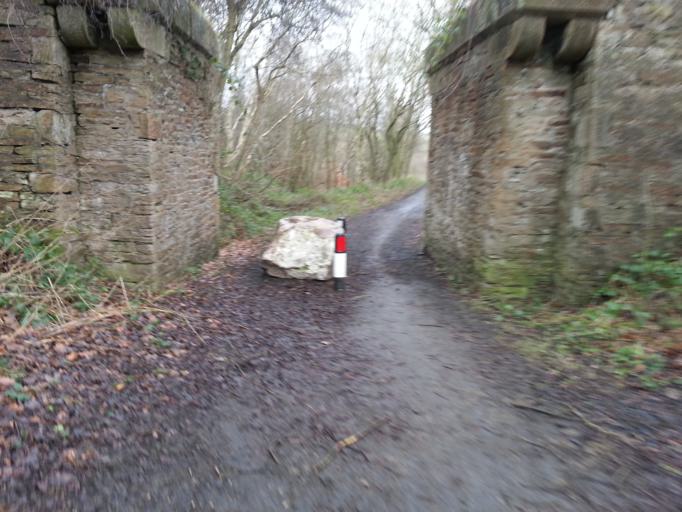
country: GB
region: England
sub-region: County Durham
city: Crook
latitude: 54.7562
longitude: -1.7313
